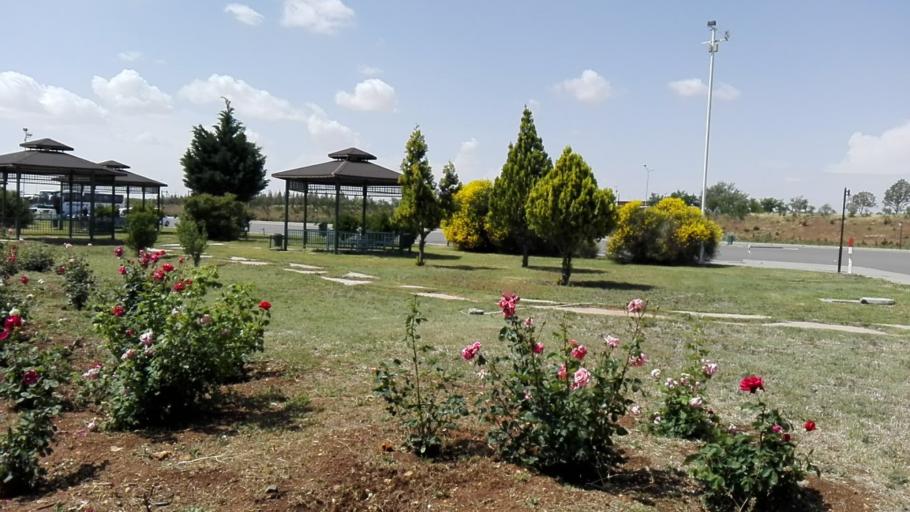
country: TR
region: Sanliurfa
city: Bogurtlen
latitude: 37.0982
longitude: 38.1900
